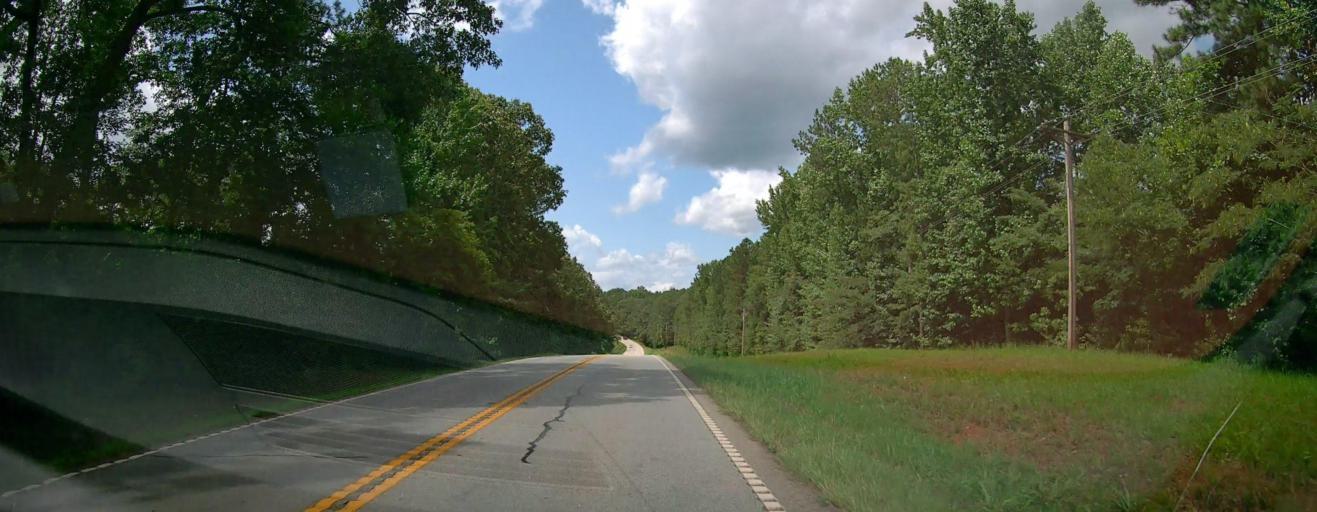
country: US
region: Georgia
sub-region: Heard County
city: Franklin
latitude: 33.3061
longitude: -85.1389
